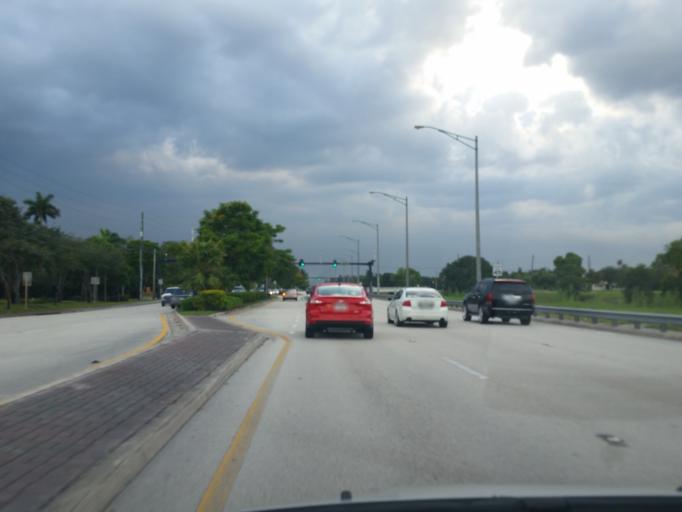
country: US
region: Florida
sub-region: Broward County
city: Cooper City
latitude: 26.0645
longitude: -80.2618
